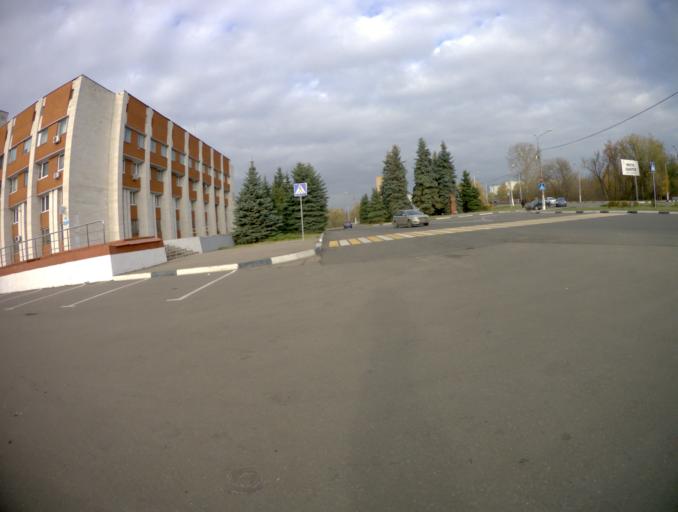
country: RU
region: Moskovskaya
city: Orekhovo-Zuyevo
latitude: 55.8068
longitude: 38.9813
